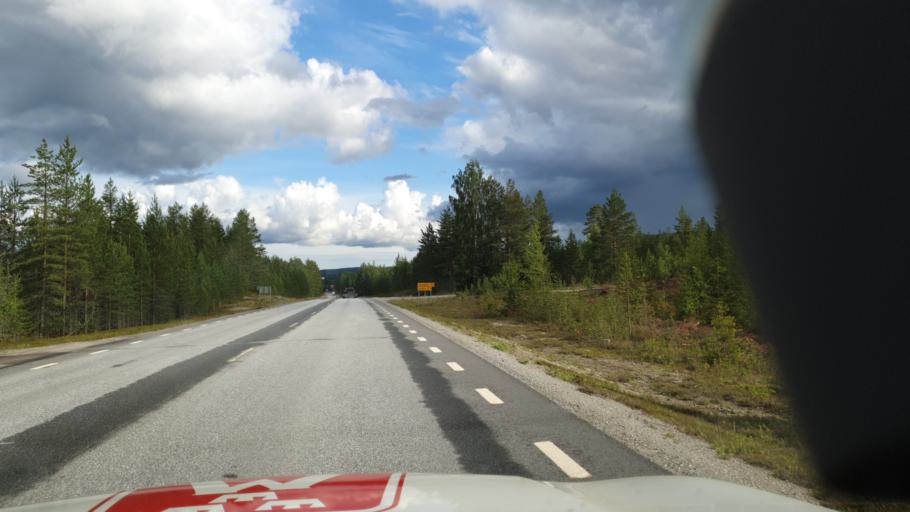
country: SE
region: Vaesterbotten
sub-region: Vannas Kommun
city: Vannasby
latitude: 64.0348
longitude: 20.0123
